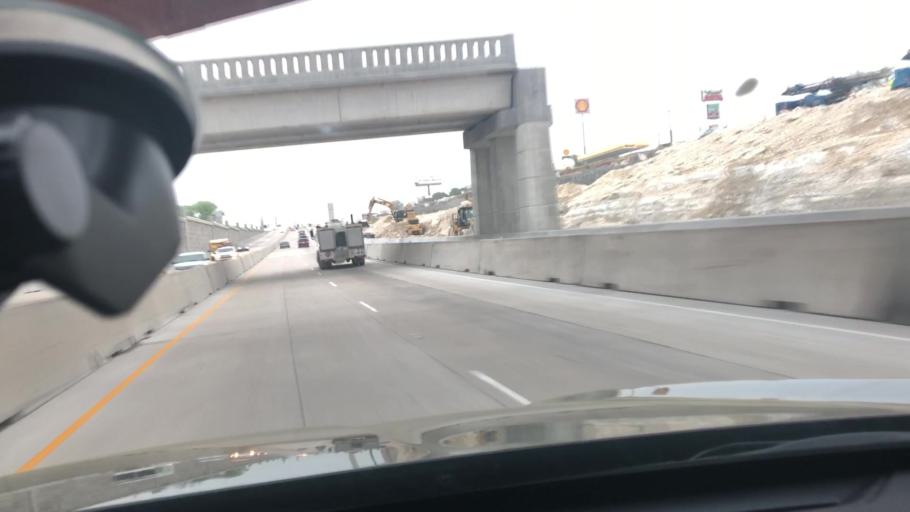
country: US
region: Texas
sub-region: Bell County
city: Temple
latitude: 31.0943
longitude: -97.3758
